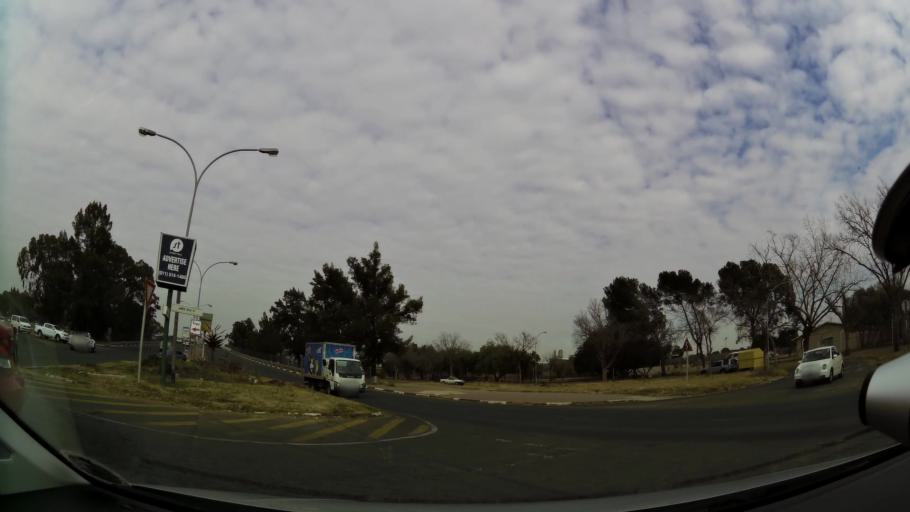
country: ZA
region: Orange Free State
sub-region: Mangaung Metropolitan Municipality
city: Bloemfontein
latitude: -29.1313
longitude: 26.2073
